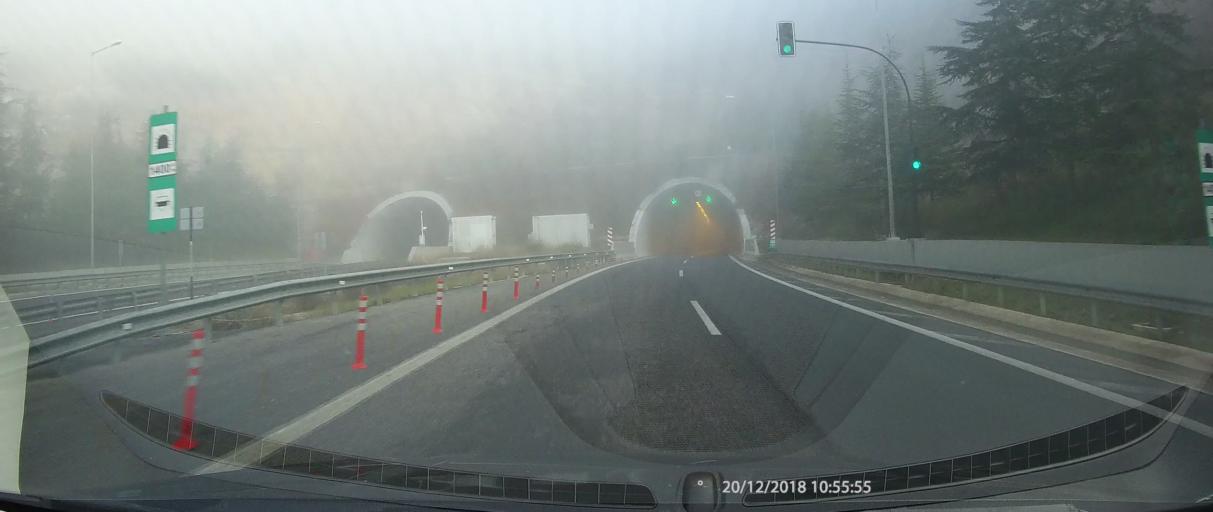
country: GR
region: Peloponnese
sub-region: Nomos Arkadias
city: Tripoli
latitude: 37.6564
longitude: 22.4685
